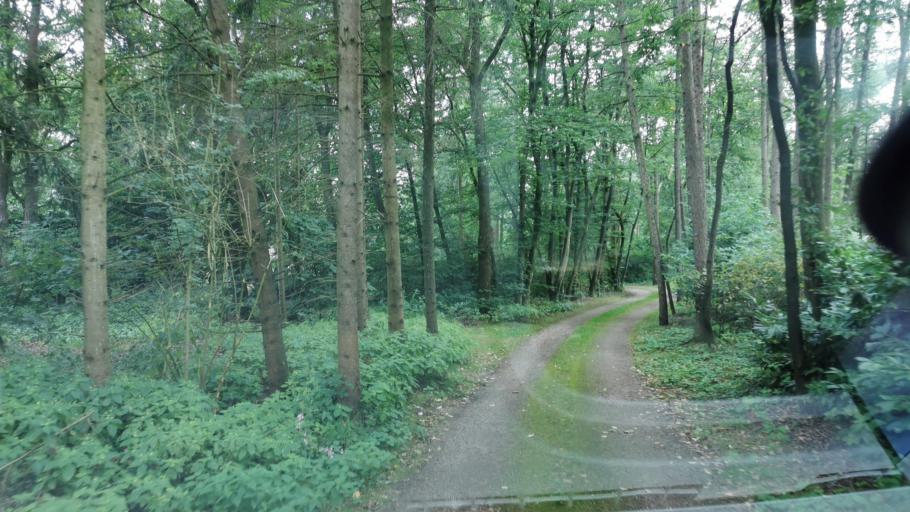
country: NL
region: Overijssel
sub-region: Gemeente Enschede
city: Enschede
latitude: 52.1468
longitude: 6.8474
